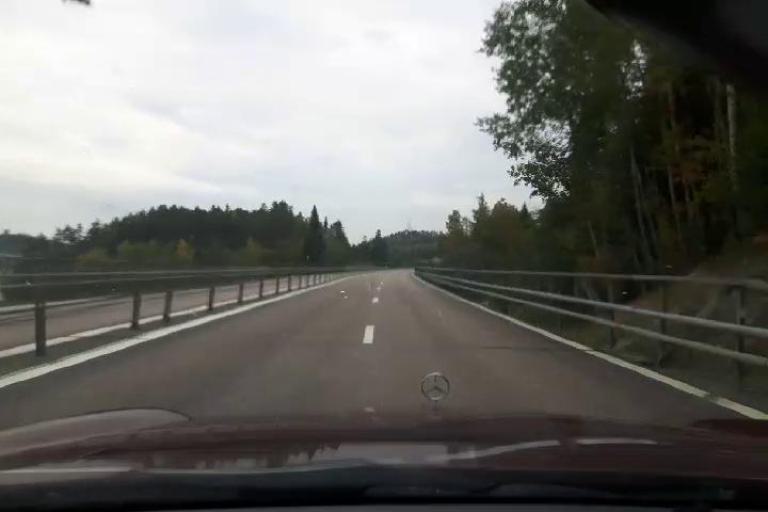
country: SE
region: Vaesternorrland
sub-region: Haernoesands Kommun
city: Haernoesand
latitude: 62.8182
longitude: 17.9691
